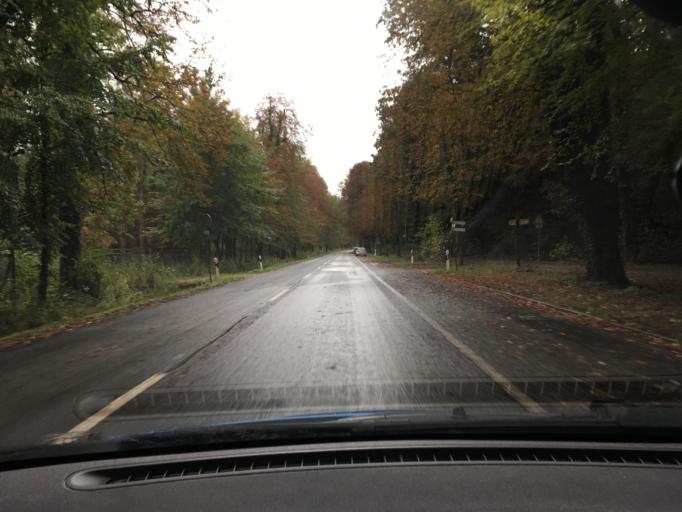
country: DE
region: Lower Saxony
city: Springe
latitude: 52.1874
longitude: 9.6039
